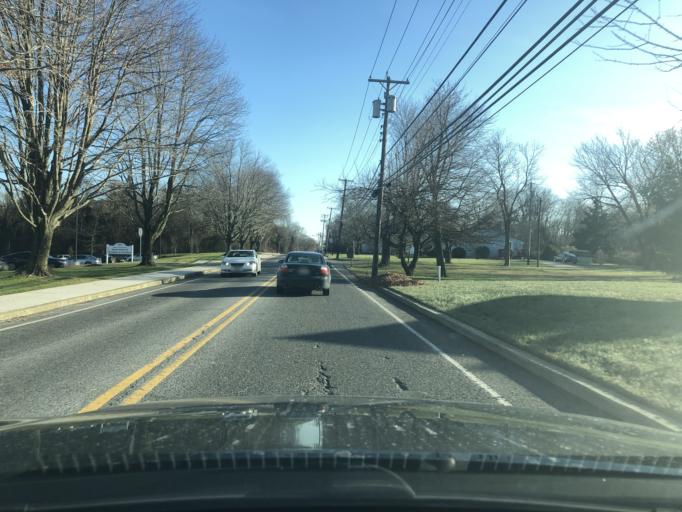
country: US
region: New Jersey
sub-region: Atlantic County
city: Northfield
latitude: 39.3914
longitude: -74.5508
